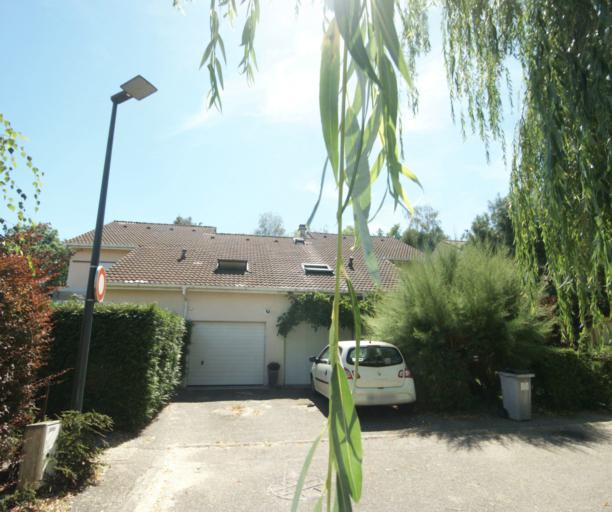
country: FR
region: Lorraine
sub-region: Departement des Vosges
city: Epinal
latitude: 48.1900
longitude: 6.4526
